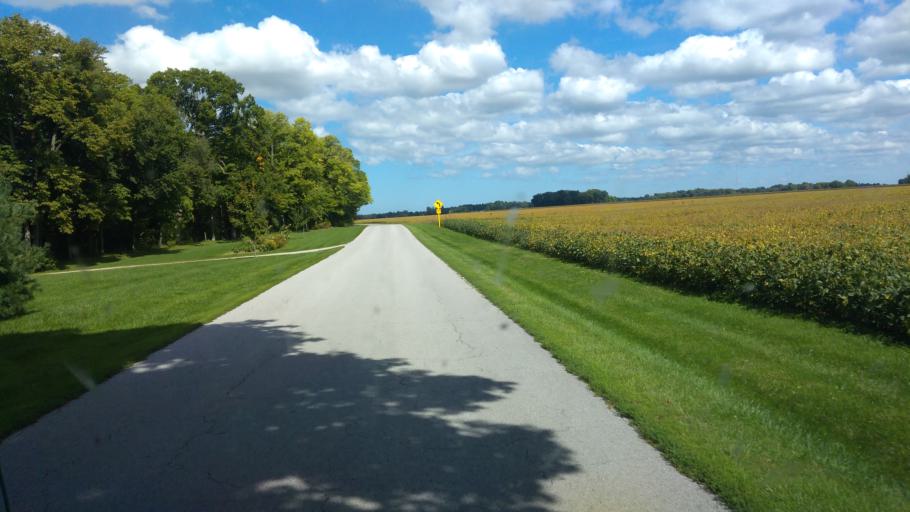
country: US
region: Ohio
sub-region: Huron County
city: Monroeville
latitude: 41.2740
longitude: -82.6755
